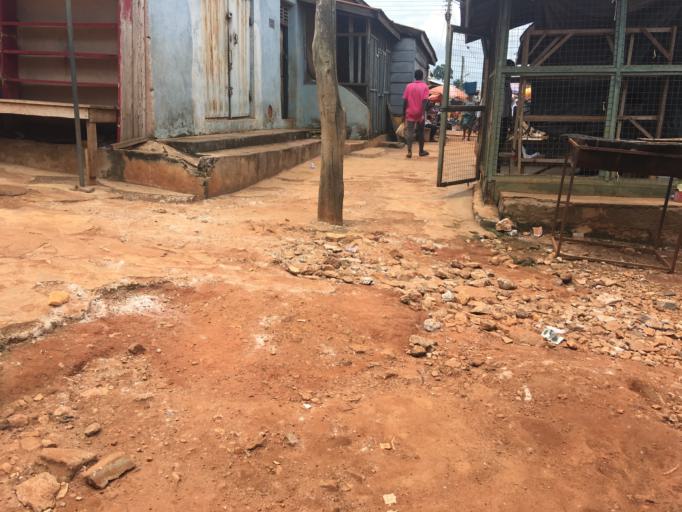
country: GH
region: Western
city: Bibiani
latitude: 6.8045
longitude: -2.5161
